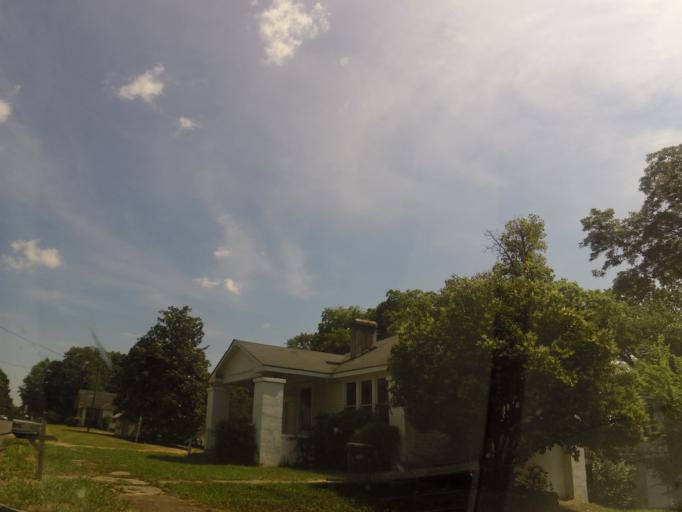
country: US
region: Mississippi
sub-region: Lauderdale County
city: Meridian
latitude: 32.3781
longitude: -88.7013
